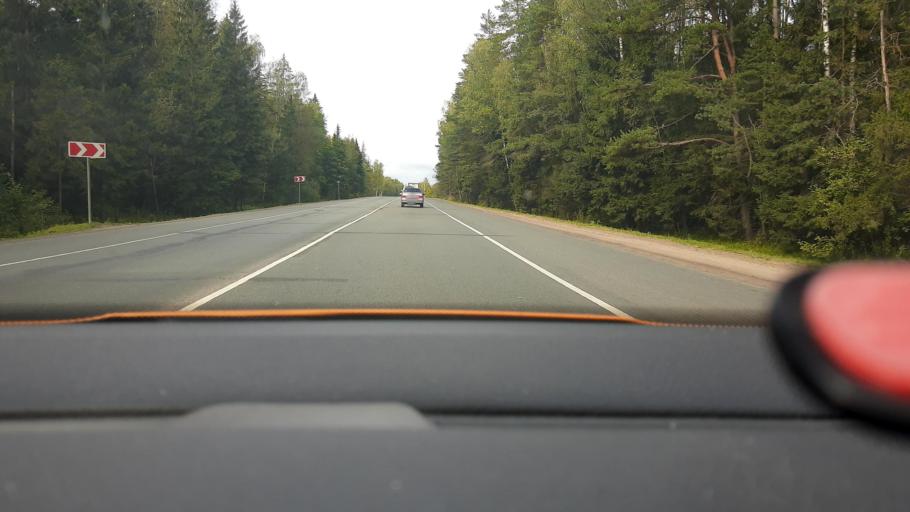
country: RU
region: Moskovskaya
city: Zelenogradskiy
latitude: 56.0854
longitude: 37.9987
